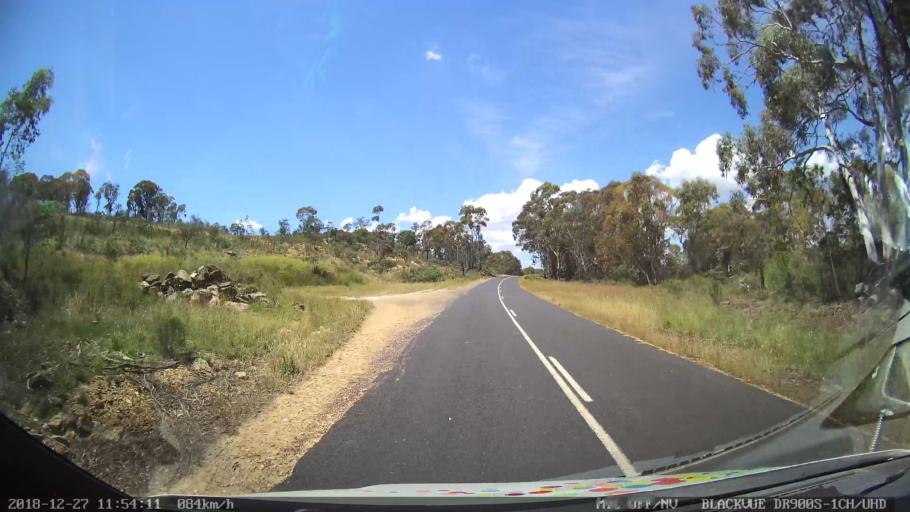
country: AU
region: New South Wales
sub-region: Blayney
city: Blayney
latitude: -33.6716
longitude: 149.4023
